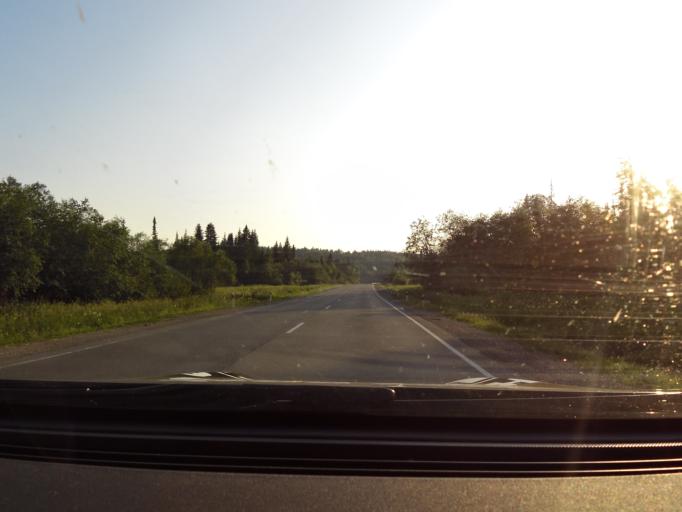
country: RU
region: Sverdlovsk
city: Mikhaylovsk
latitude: 56.5113
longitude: 59.1773
